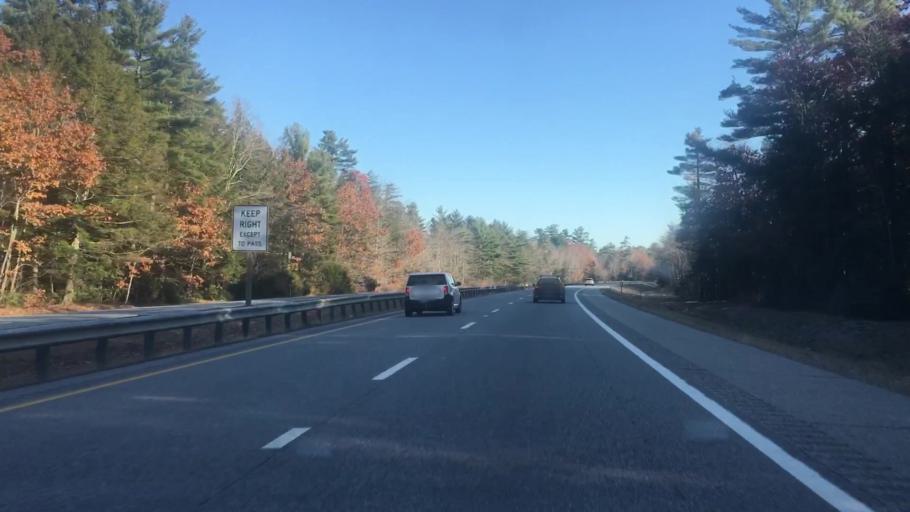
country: US
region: Maine
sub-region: Cumberland County
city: New Gloucester
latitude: 43.9694
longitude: -70.3238
